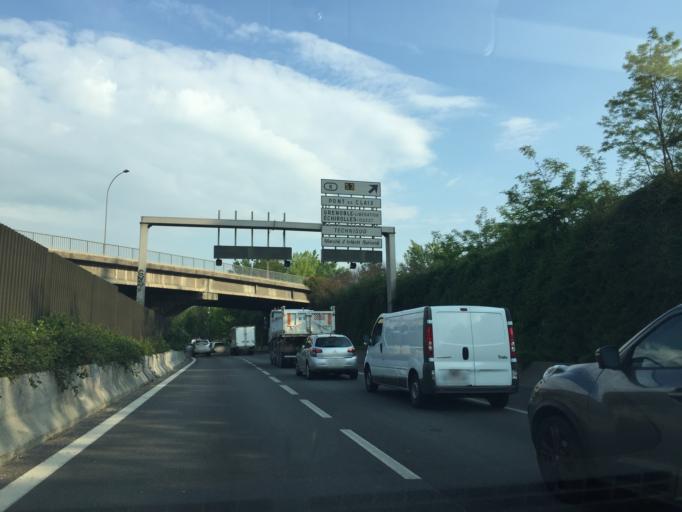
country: FR
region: Rhone-Alpes
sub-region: Departement de l'Isere
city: Grenoble
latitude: 45.1562
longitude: 5.7134
